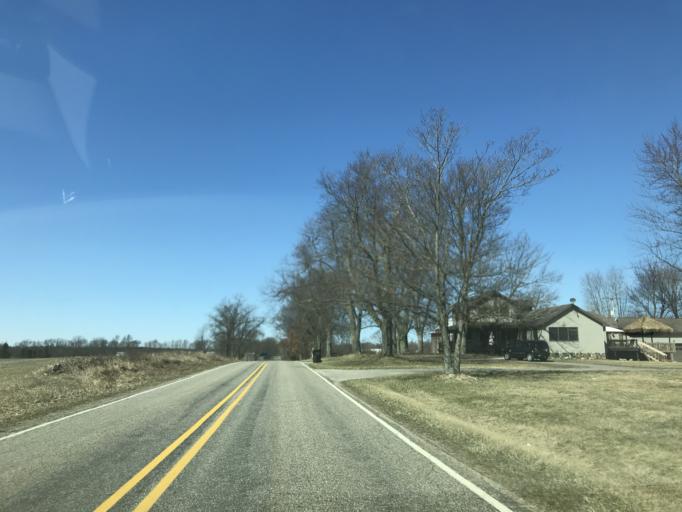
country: US
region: Michigan
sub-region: Hillsdale County
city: Litchfield
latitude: 41.9855
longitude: -84.7299
